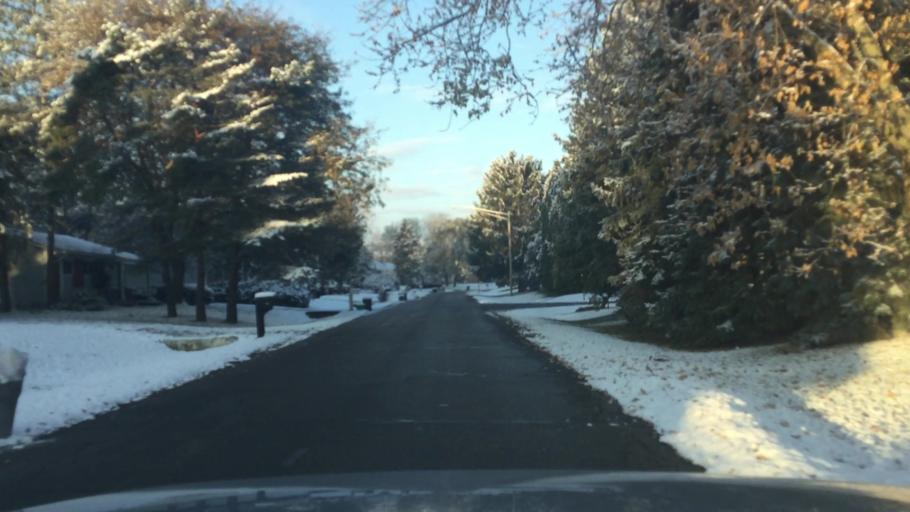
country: US
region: Michigan
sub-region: Oakland County
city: Walled Lake
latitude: 42.5445
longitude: -83.4846
